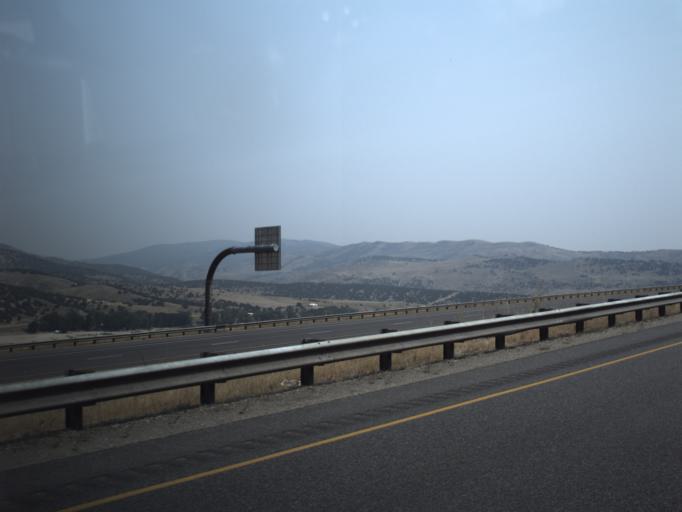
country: US
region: Utah
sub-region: Summit County
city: Coalville
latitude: 40.9589
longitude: -111.4272
